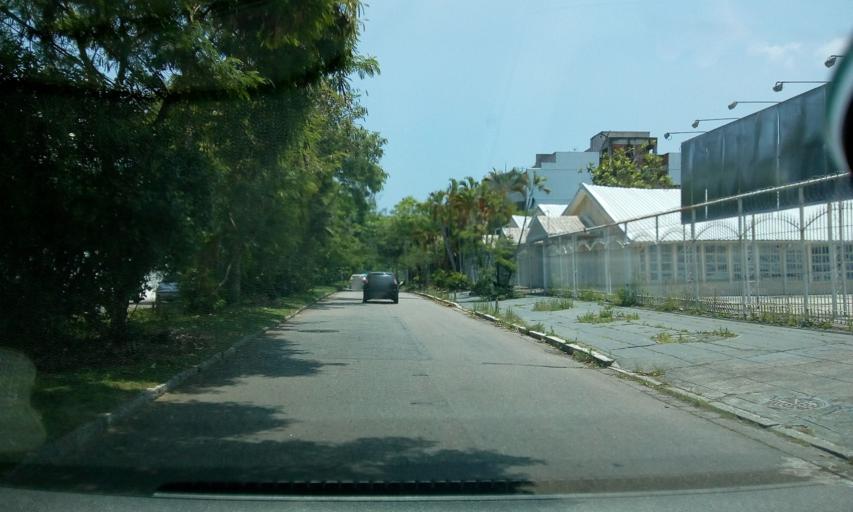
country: BR
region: Rio de Janeiro
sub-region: Nilopolis
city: Nilopolis
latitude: -23.0187
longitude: -43.4676
